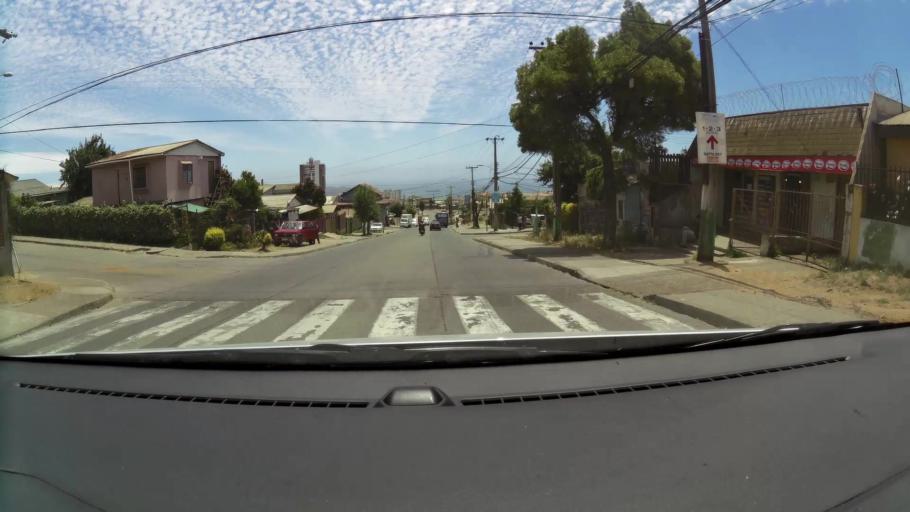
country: CL
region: Valparaiso
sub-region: Provincia de Valparaiso
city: Vina del Mar
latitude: -33.0502
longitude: -71.5741
